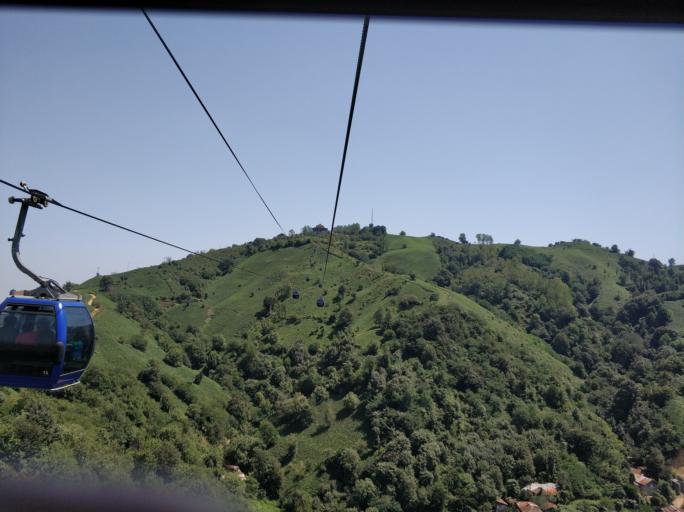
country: IR
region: Gilan
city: Lahijan
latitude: 37.1990
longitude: 50.0312
